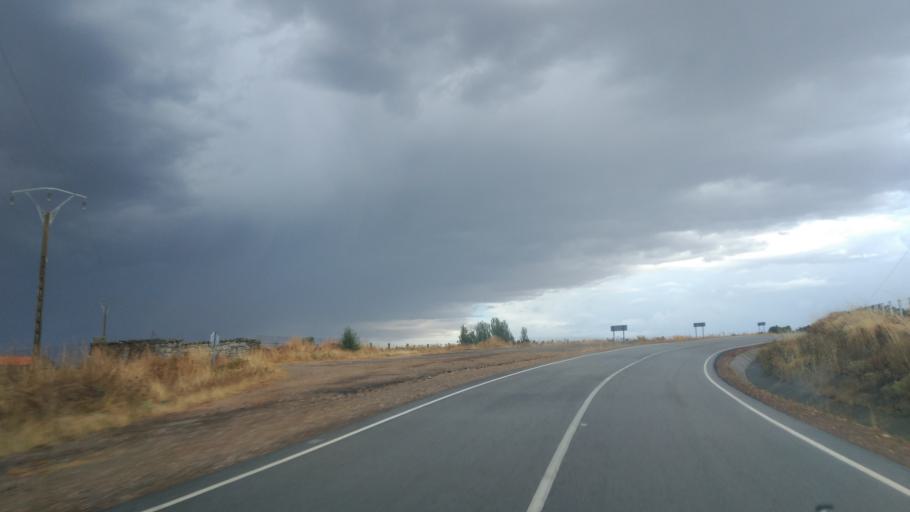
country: ES
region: Castille and Leon
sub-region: Provincia de Salamanca
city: Aldeanueva de la Sierra
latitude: 40.6062
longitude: -6.1358
